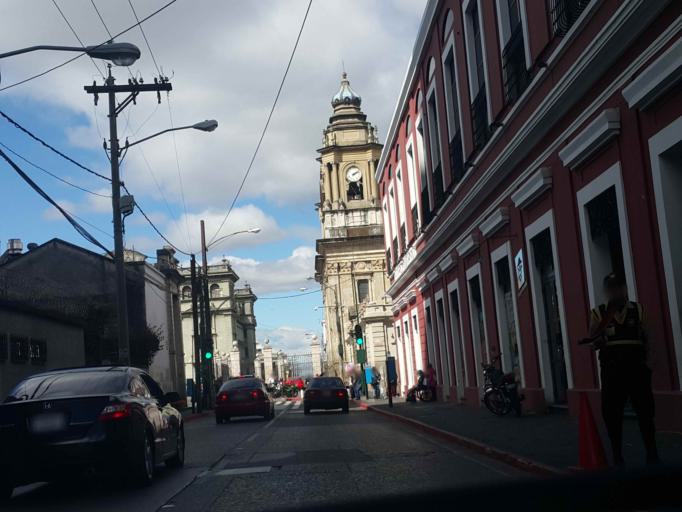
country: GT
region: Guatemala
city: Guatemala City
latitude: 14.6406
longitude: -90.5127
